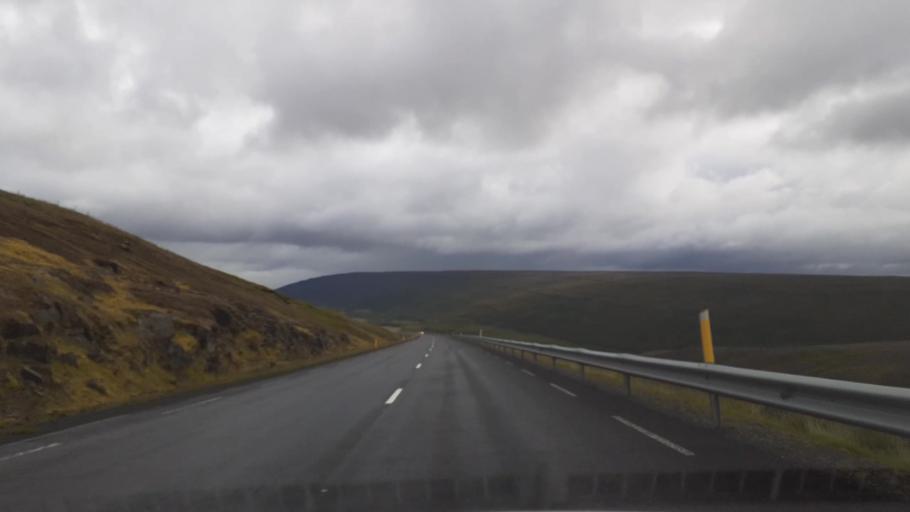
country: IS
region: East
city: Egilsstadir
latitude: 65.3022
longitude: -15.2037
